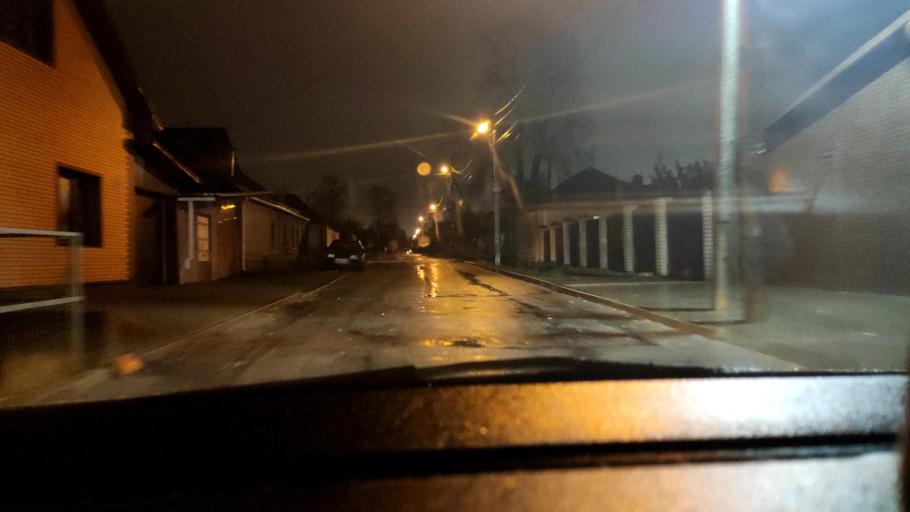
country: RU
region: Voronezj
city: Voronezh
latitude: 51.6352
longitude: 39.1623
